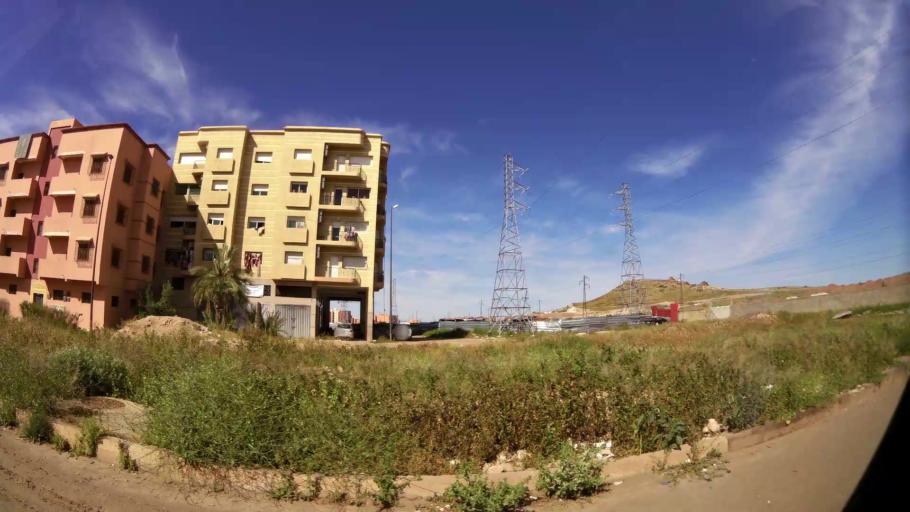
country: MA
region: Marrakech-Tensift-Al Haouz
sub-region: Marrakech
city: Marrakesh
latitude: 31.6675
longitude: -8.0223
